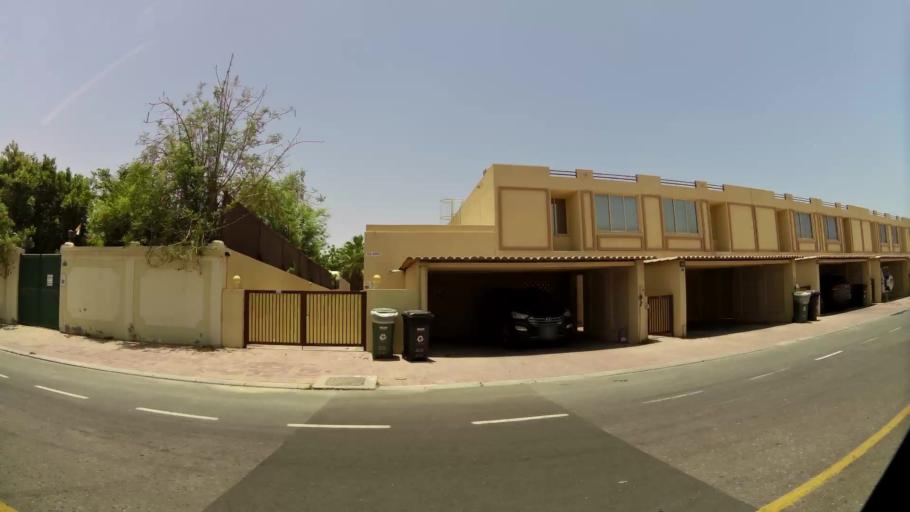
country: AE
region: Dubai
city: Dubai
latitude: 25.1745
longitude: 55.2218
